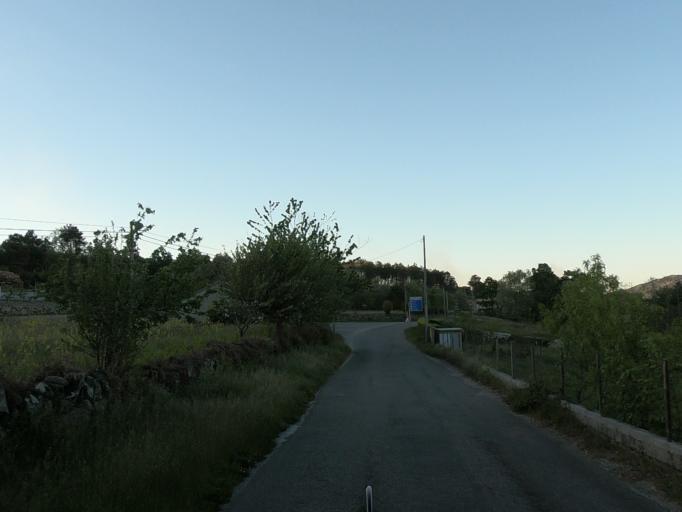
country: PT
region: Vila Real
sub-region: Sabrosa
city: Sabrosa
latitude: 41.3424
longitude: -7.6233
